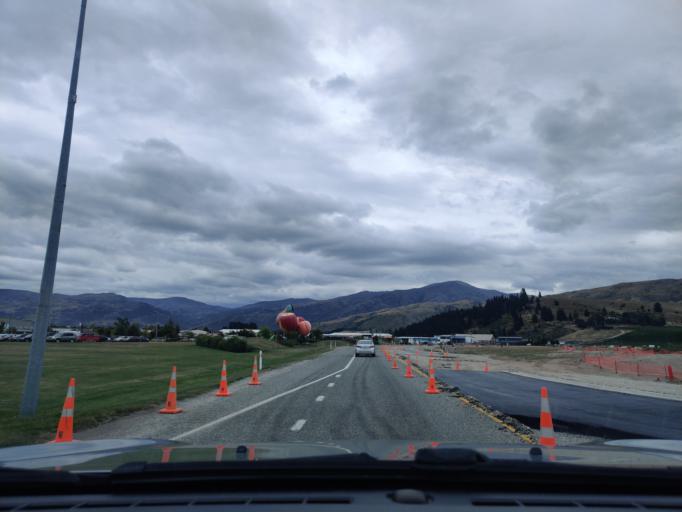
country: NZ
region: Otago
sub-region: Queenstown-Lakes District
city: Wanaka
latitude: -45.0350
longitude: 169.1992
